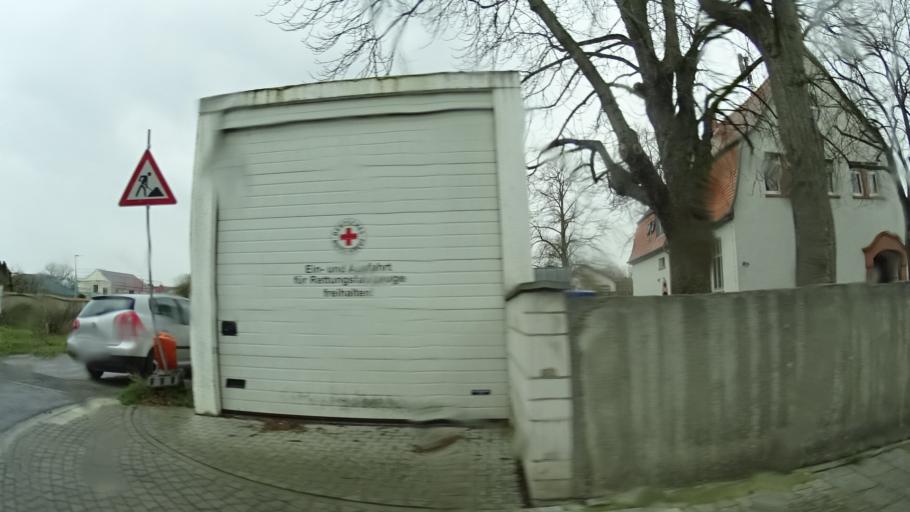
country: DE
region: Hesse
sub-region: Regierungsbezirk Darmstadt
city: Riedstadt
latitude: 49.8370
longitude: 8.4690
